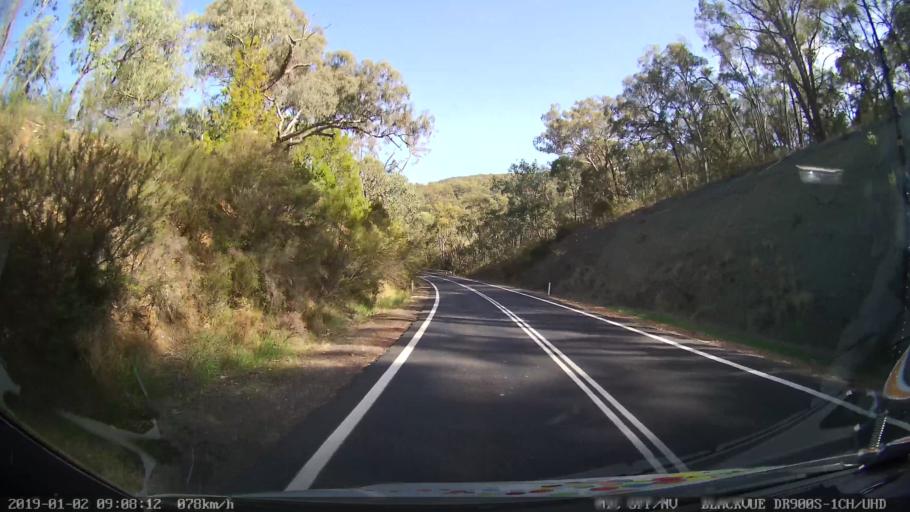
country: AU
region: New South Wales
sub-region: Tumut Shire
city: Tumut
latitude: -35.5326
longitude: 148.2943
